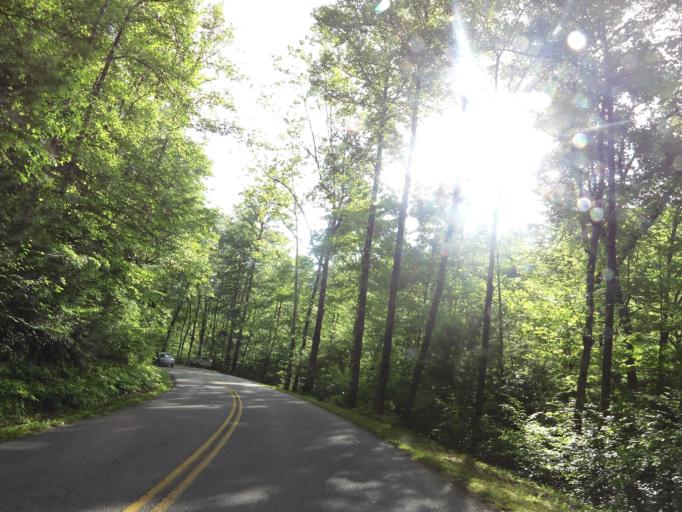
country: US
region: Tennessee
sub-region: Sevier County
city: Gatlinburg
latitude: 35.6813
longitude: -83.6520
